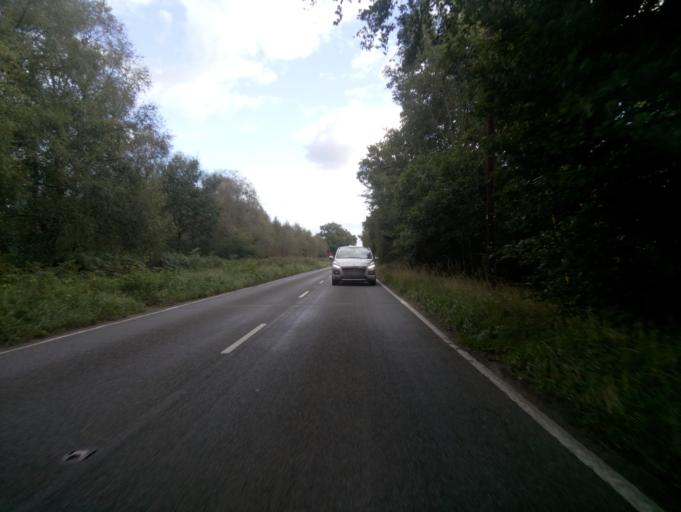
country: GB
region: England
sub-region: Devon
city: Honiton
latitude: 50.7618
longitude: -3.2129
